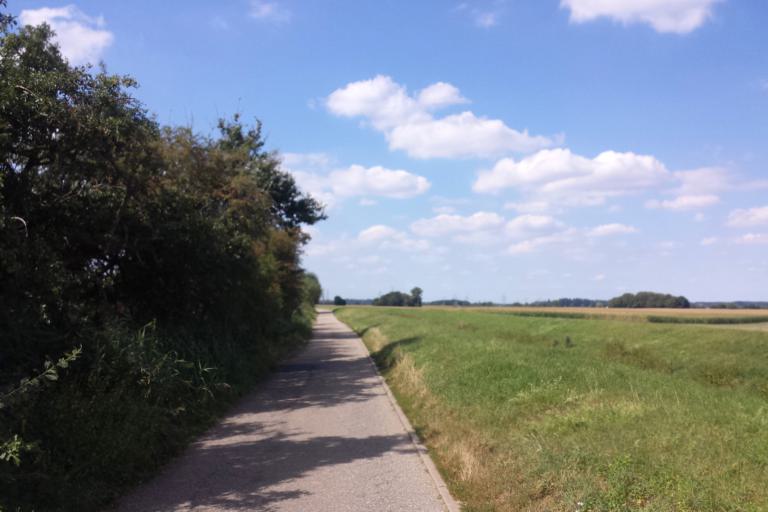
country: DE
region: Baden-Wuerttemberg
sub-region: Karlsruhe Region
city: Hemsbach
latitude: 49.5748
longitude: 8.6283
